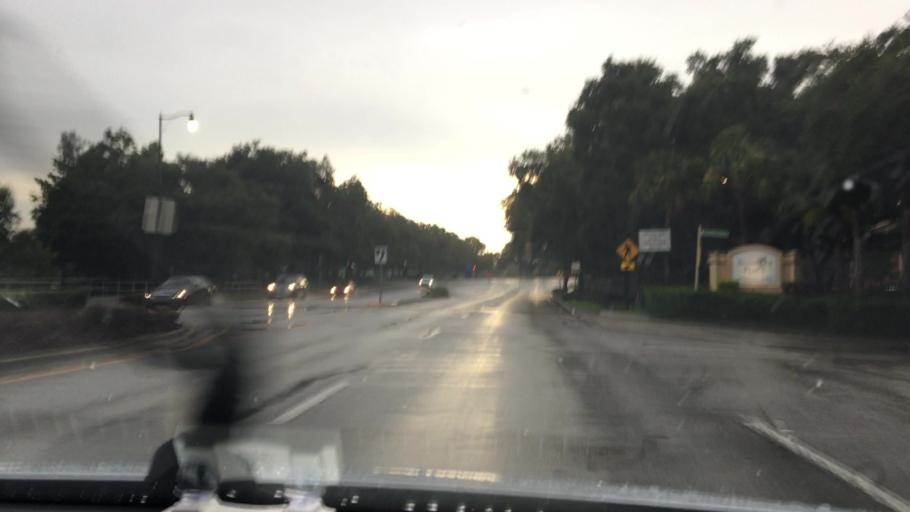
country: US
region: Florida
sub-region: Seminole County
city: Altamonte Springs
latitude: 28.6692
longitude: -81.3818
